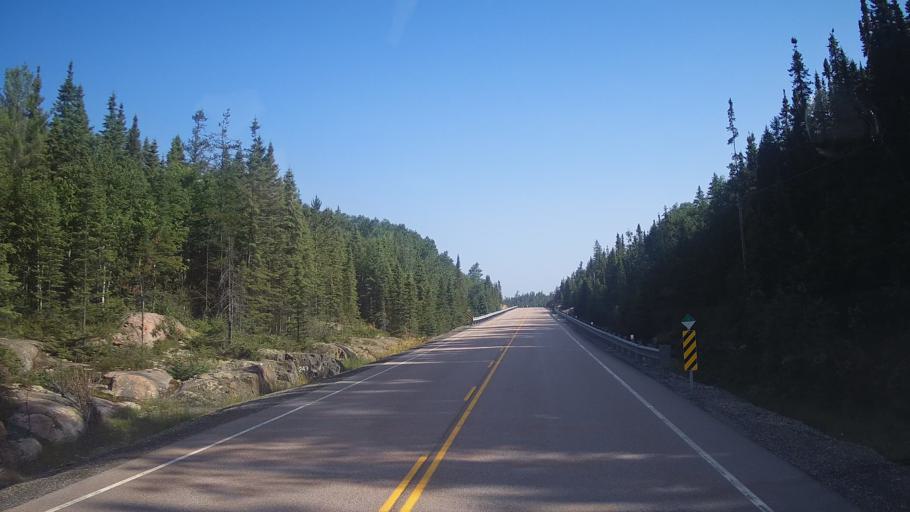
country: CA
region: Ontario
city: Rayside-Balfour
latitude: 47.0049
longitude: -81.6330
